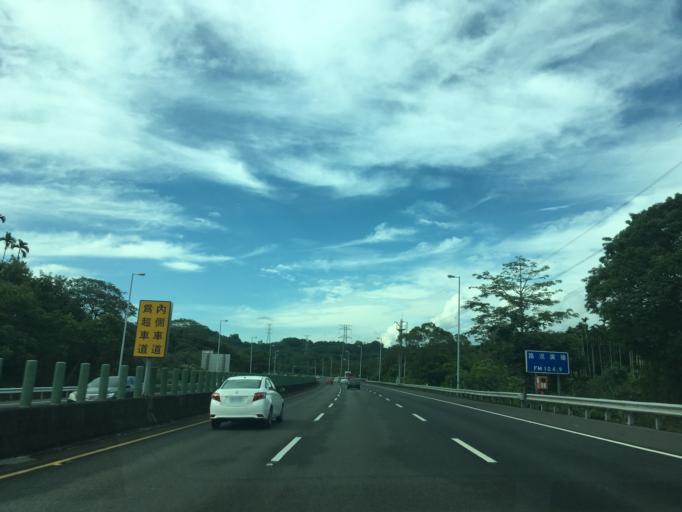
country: TW
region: Taiwan
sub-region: Chiayi
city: Jiayi Shi
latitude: 23.4667
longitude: 120.4983
